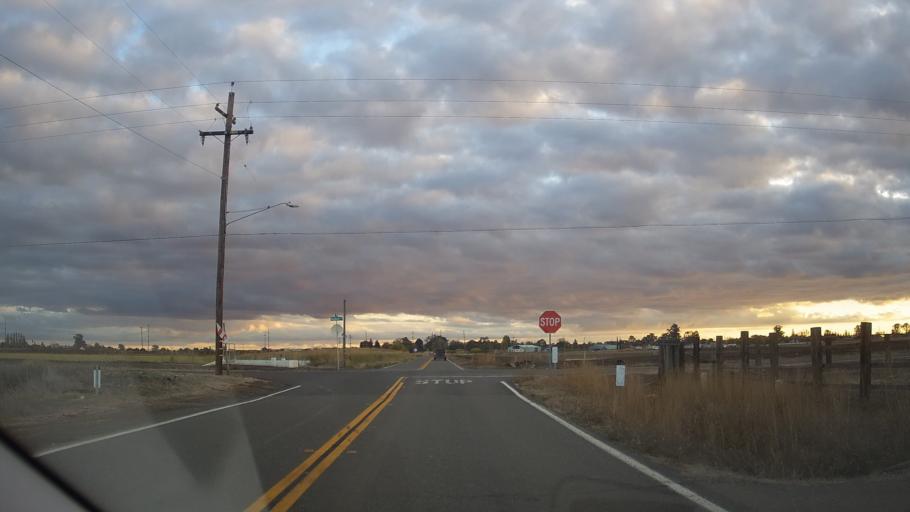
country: US
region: California
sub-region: Solano County
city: Hartley
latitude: 38.3593
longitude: -121.9061
